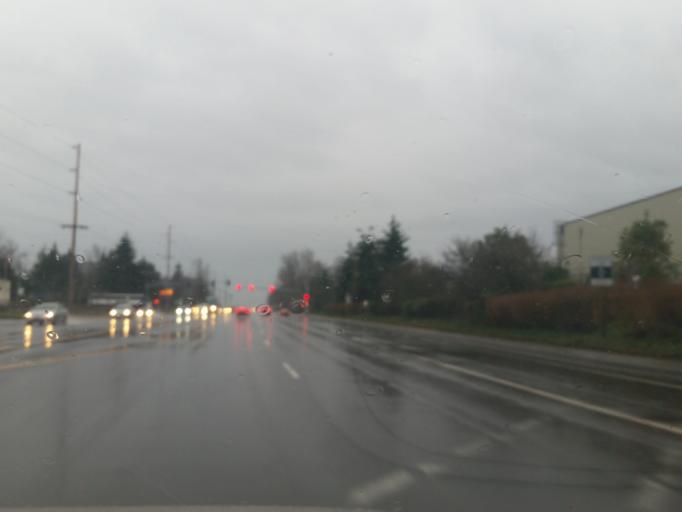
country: US
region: Washington
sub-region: Snohomish County
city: Mukilteo
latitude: 47.9199
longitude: -122.2718
